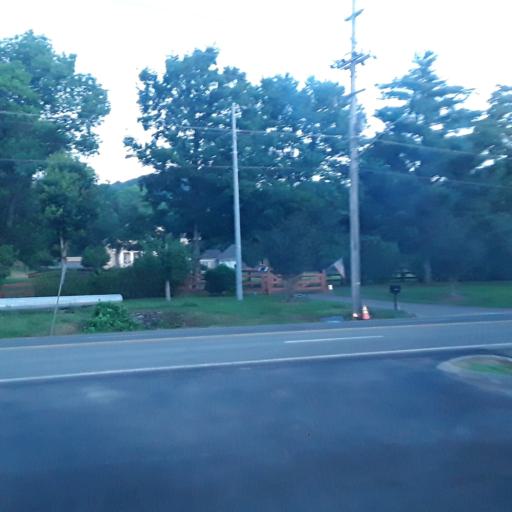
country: US
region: Tennessee
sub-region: Davidson County
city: Oak Hill
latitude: 36.0647
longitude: -86.7740
